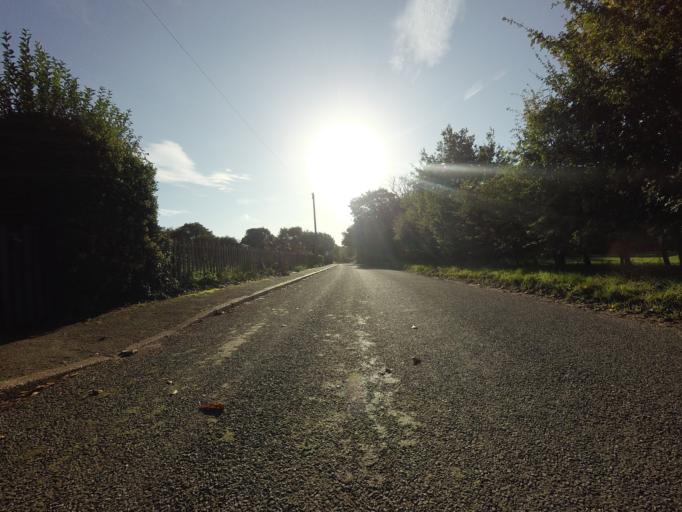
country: GB
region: England
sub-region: Norfolk
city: Dersingham
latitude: 52.8354
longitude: 0.5827
